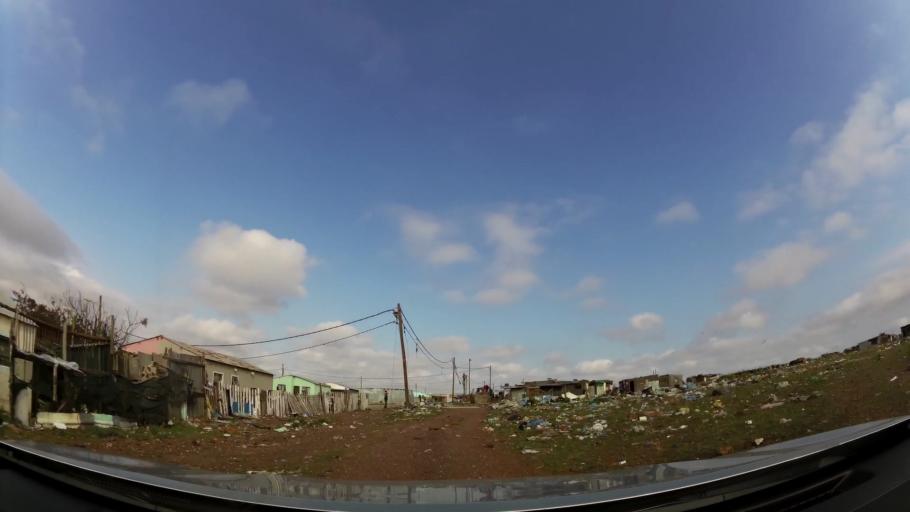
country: ZA
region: Eastern Cape
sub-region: Nelson Mandela Bay Metropolitan Municipality
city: Port Elizabeth
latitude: -33.9151
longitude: 25.5401
